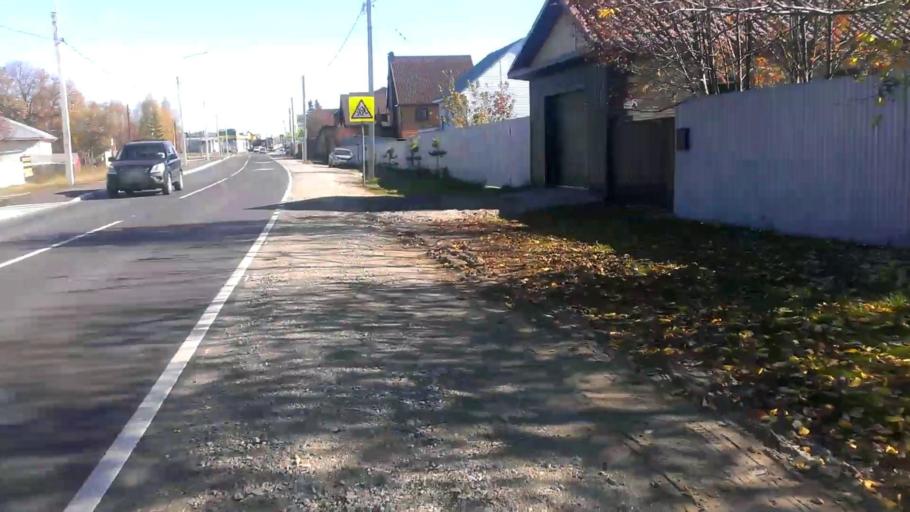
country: RU
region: Altai Krai
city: Sannikovo
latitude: 53.3173
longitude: 83.9512
